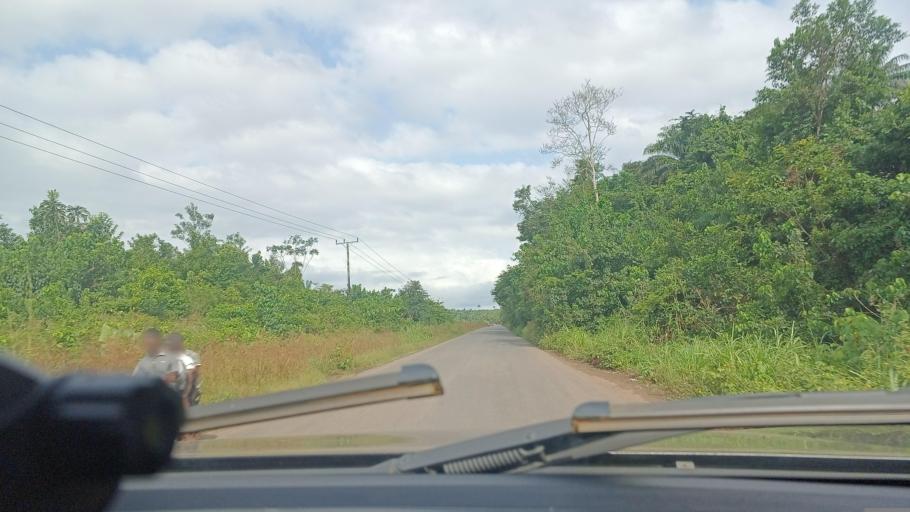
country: LR
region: Bomi
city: Tubmanburg
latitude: 6.7276
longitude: -10.9876
